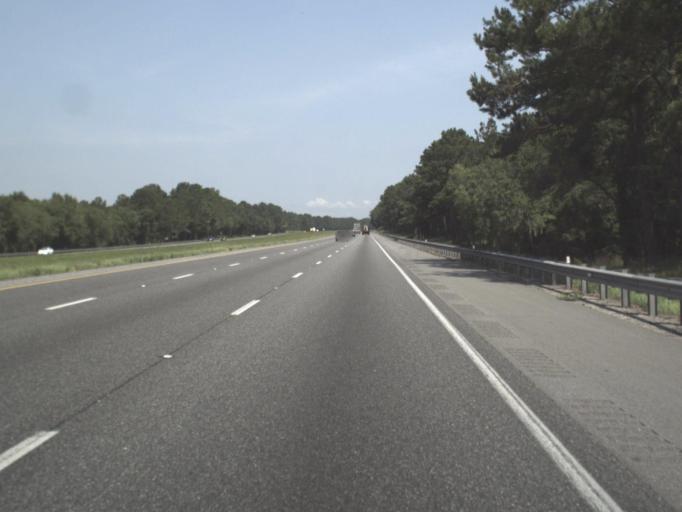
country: US
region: Florida
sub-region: Suwannee County
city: Wellborn
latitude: 30.3600
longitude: -82.8453
